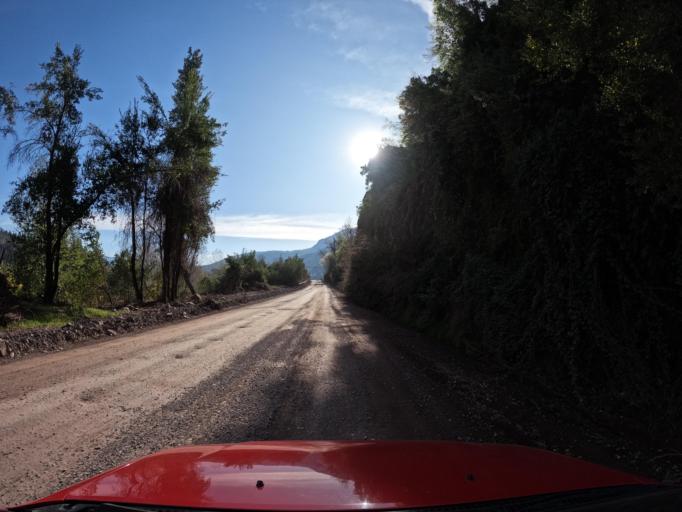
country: CL
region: O'Higgins
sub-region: Provincia de Colchagua
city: Chimbarongo
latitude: -34.9975
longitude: -70.8083
